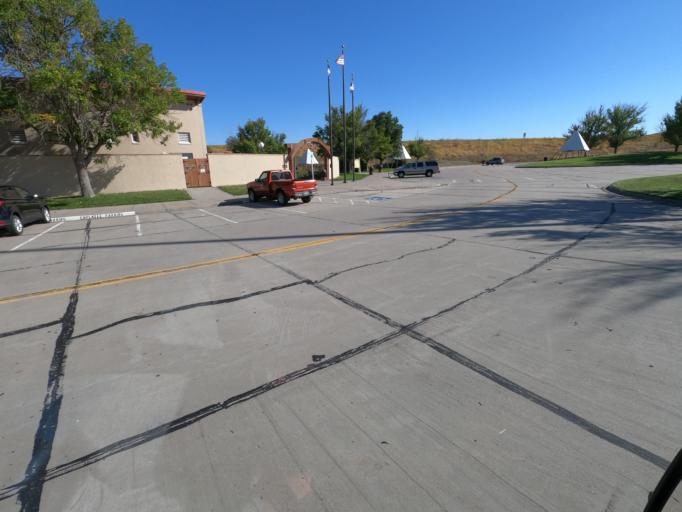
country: US
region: Colorado
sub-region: Sedgwick County
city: Julesburg
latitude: 40.9663
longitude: -102.2519
